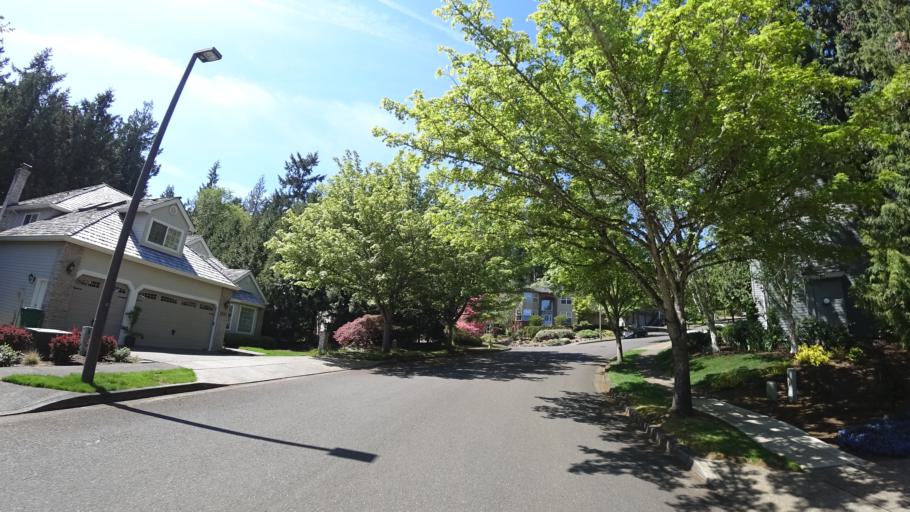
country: US
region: Oregon
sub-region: Washington County
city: Aloha
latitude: 45.4436
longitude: -122.8443
